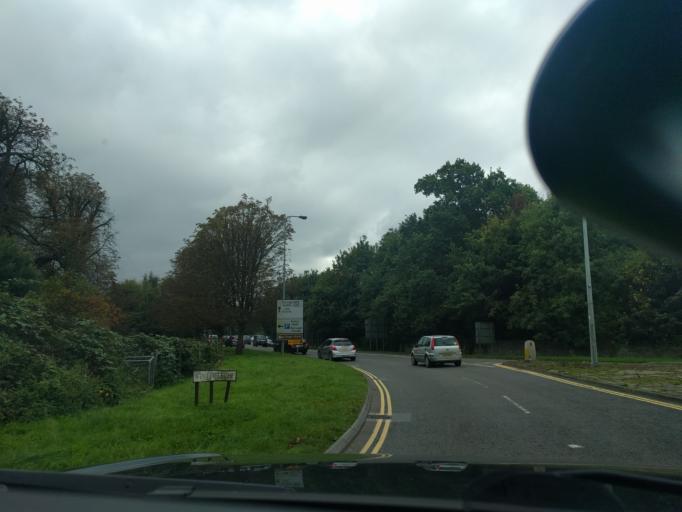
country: GB
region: England
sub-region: Wiltshire
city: Chippenham
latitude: 51.4585
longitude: -2.1191
